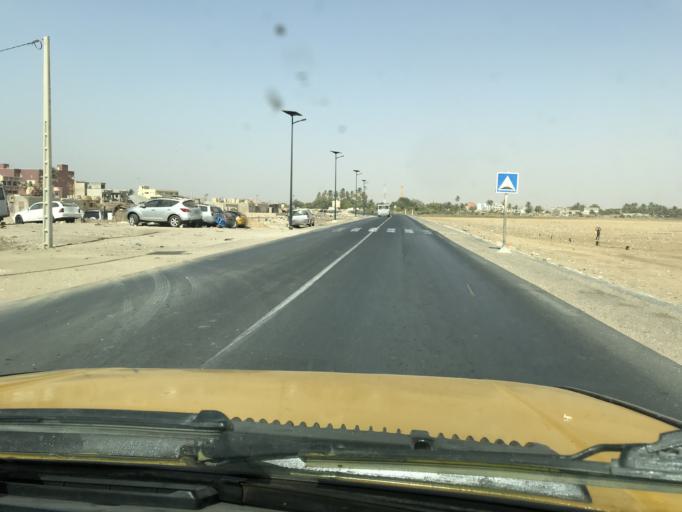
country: SN
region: Saint-Louis
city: Saint-Louis
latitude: 16.0245
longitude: -16.4810
